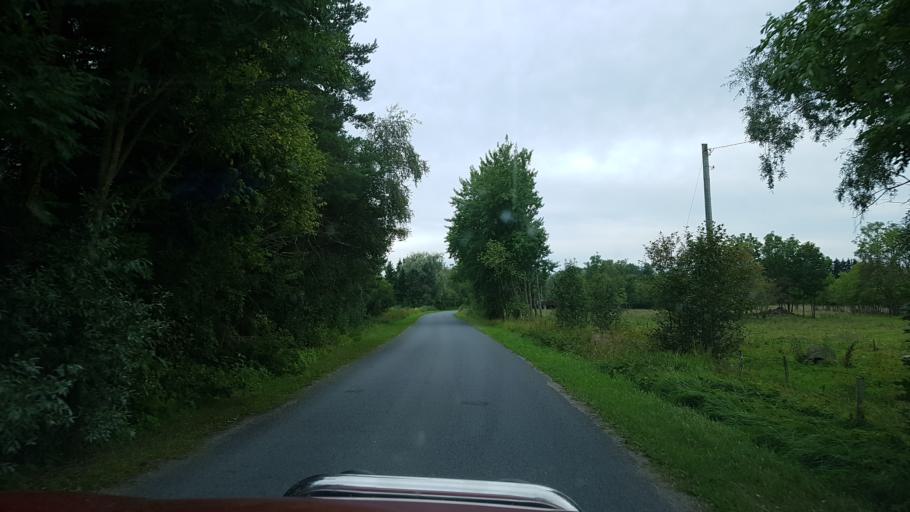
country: EE
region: Laeaene
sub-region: Ridala Parish
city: Uuemoisa
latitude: 58.8066
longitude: 23.6698
